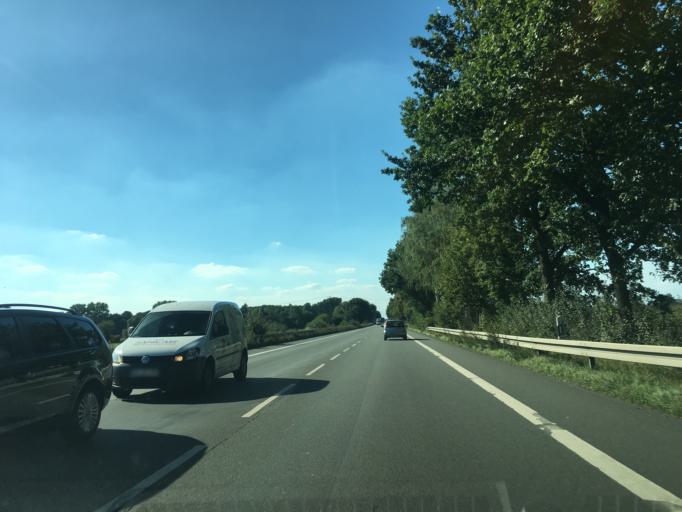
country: DE
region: North Rhine-Westphalia
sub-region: Regierungsbezirk Munster
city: Beelen
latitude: 51.9054
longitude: 8.1853
